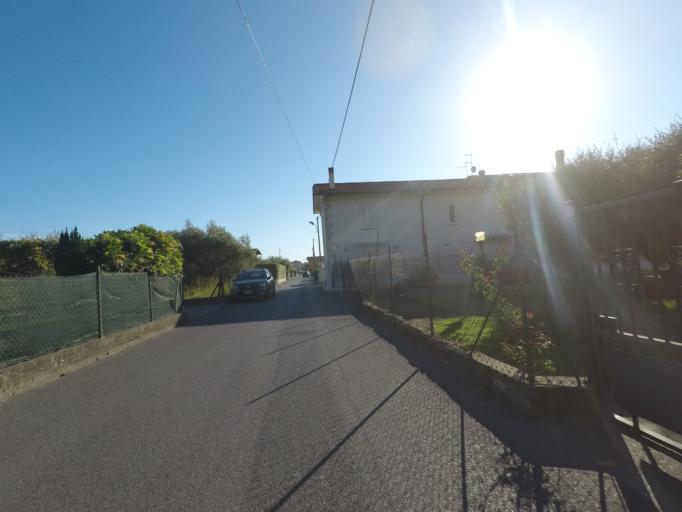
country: IT
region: Tuscany
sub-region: Provincia di Massa-Carrara
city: Capanne-Prato-Cinquale
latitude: 44.0062
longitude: 10.1533
